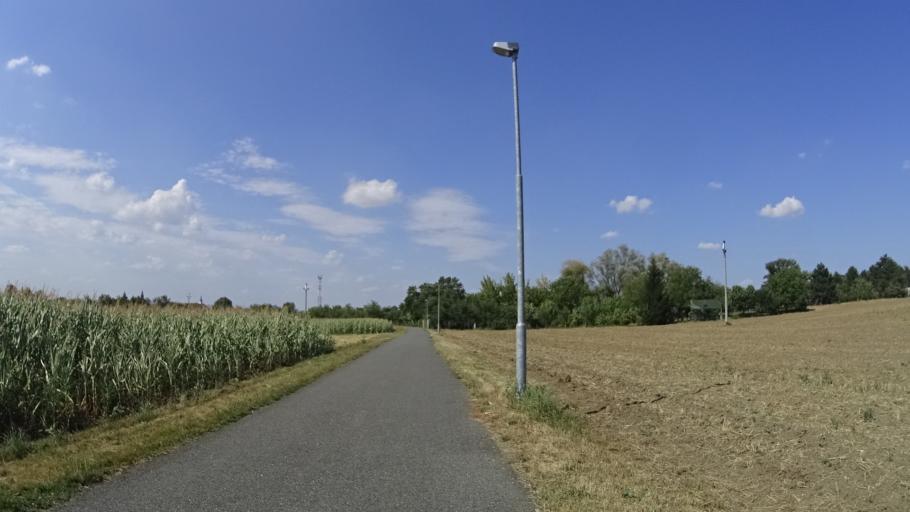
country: CZ
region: Zlin
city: Uhersky Ostroh
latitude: 48.9776
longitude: 17.3981
